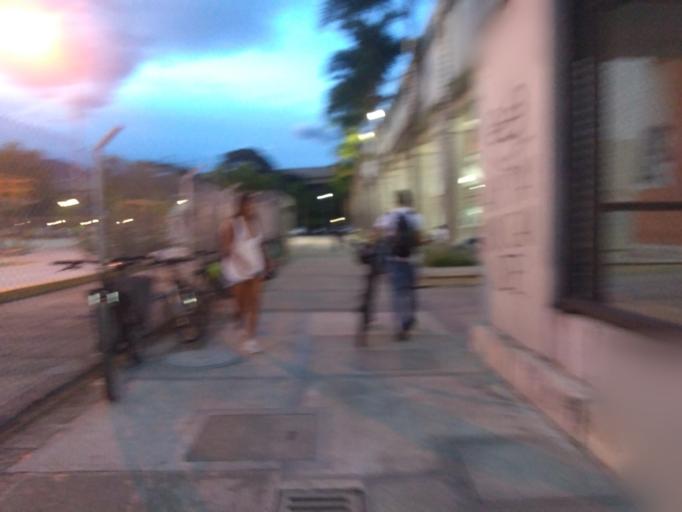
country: CO
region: Antioquia
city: Medellin
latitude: 6.2691
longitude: -75.5685
